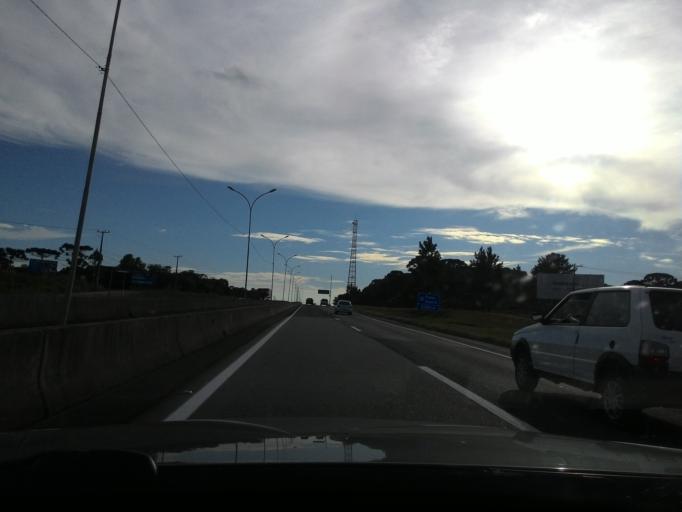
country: BR
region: Parana
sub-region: Quatro Barras
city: Quatro Barras
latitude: -25.3588
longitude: -49.0736
